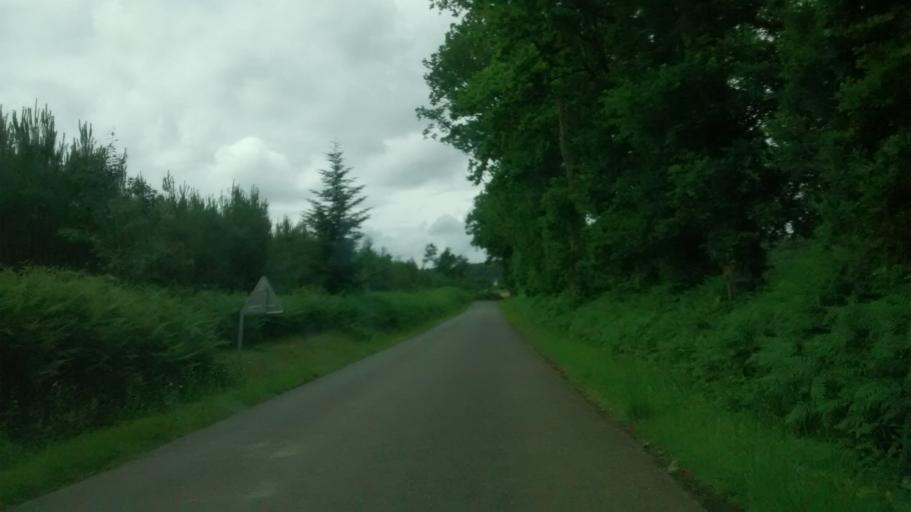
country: FR
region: Brittany
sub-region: Departement du Morbihan
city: Carentoir
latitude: 47.8349
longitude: -2.2029
